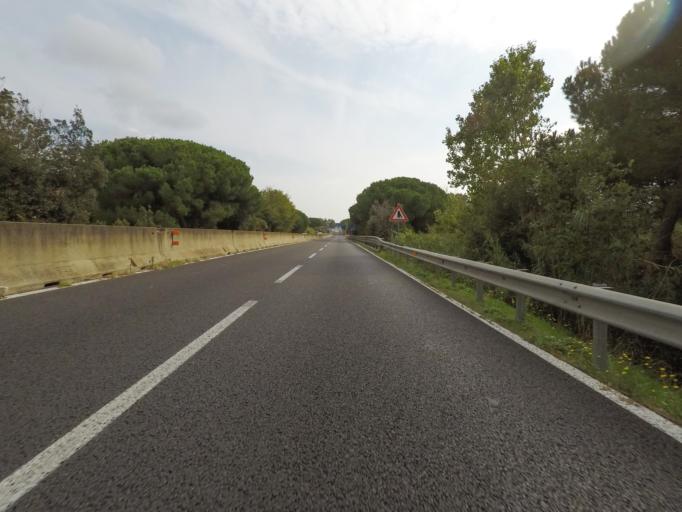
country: IT
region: Tuscany
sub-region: Provincia di Grosseto
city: Orbetello Scalo
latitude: 42.4766
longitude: 11.2316
